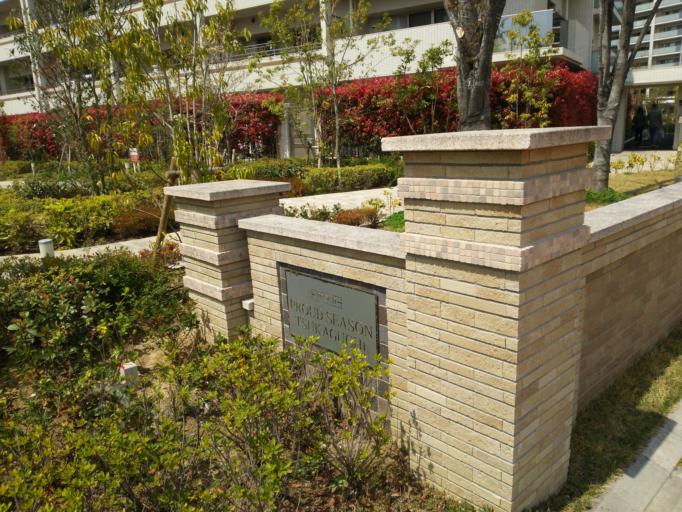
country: JP
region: Hyogo
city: Amagasaki
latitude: 34.7516
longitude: 135.4270
